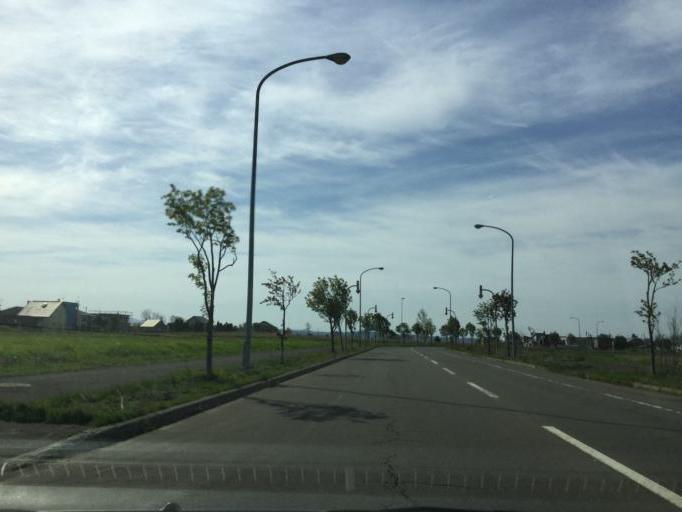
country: JP
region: Hokkaido
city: Iwamizawa
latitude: 43.1775
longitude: 141.7102
